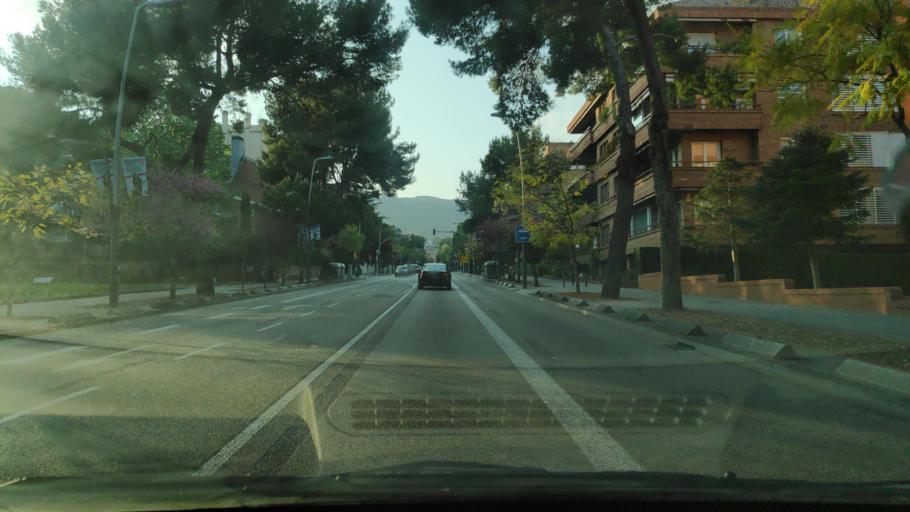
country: ES
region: Catalonia
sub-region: Provincia de Barcelona
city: les Corts
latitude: 41.3907
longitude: 2.1183
